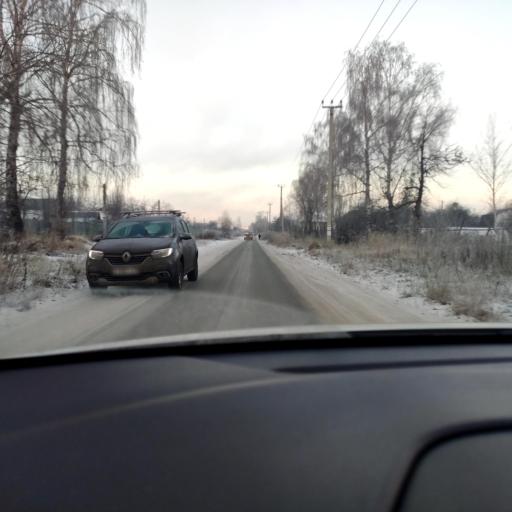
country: RU
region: Tatarstan
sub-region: Gorod Kazan'
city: Kazan
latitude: 55.8604
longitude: 49.0538
